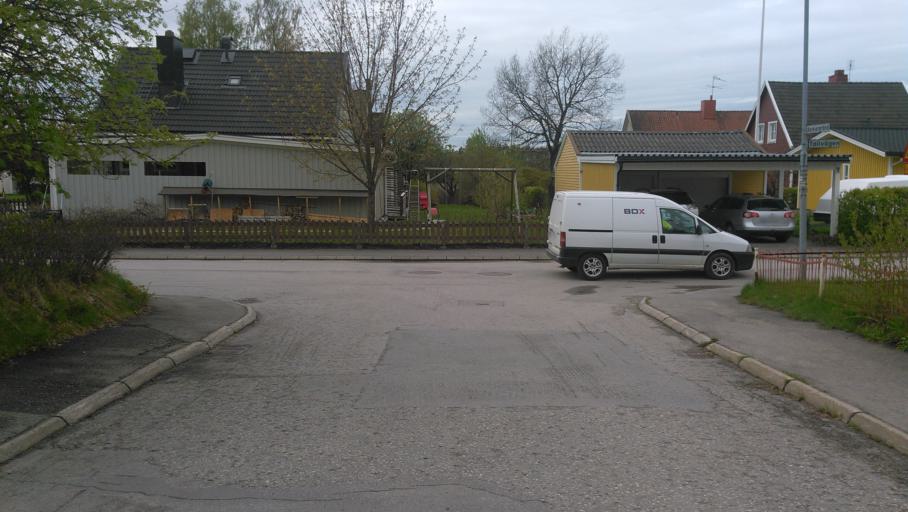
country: SE
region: Vaesterbotten
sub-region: Umea Kommun
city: Umea
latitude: 63.8058
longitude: 20.3011
